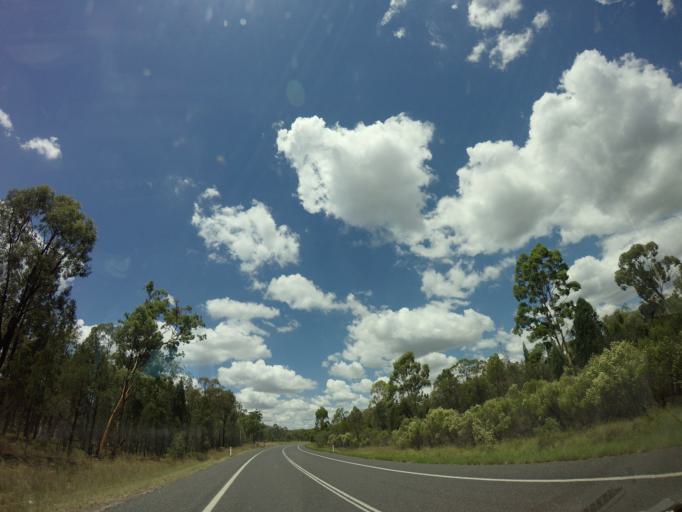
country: AU
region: Queensland
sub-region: Western Downs
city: Dalby
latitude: -27.9673
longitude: 151.0038
